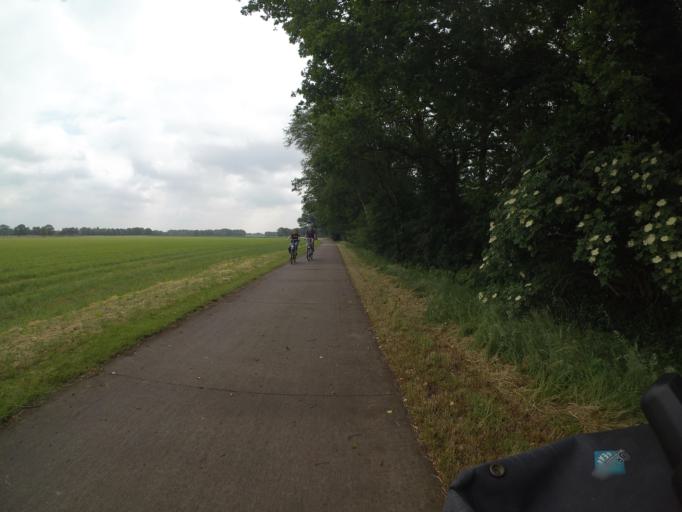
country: NL
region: Drenthe
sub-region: Gemeente Westerveld
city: Havelte
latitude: 52.8391
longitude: 6.2841
